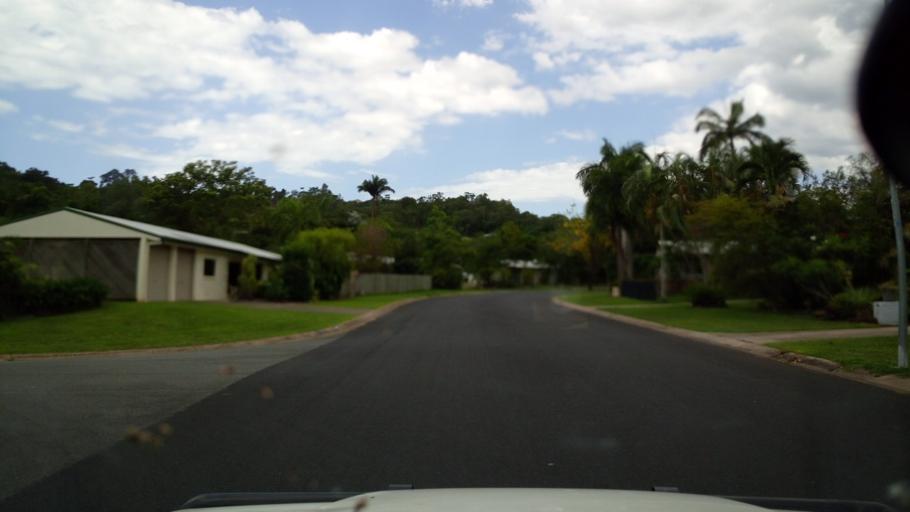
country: AU
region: Queensland
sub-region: Cairns
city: Redlynch
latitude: -16.9057
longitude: 145.7142
